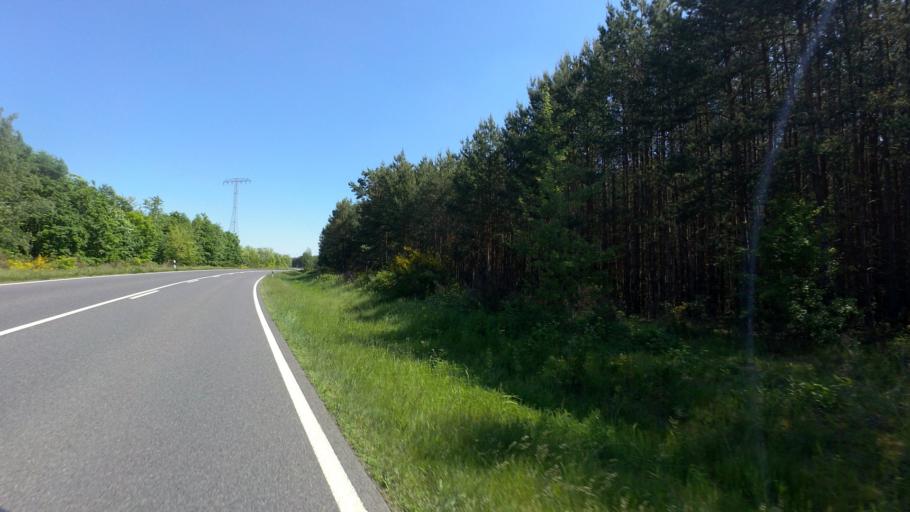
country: DE
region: Brandenburg
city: Spremberg
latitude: 51.5621
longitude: 14.3267
